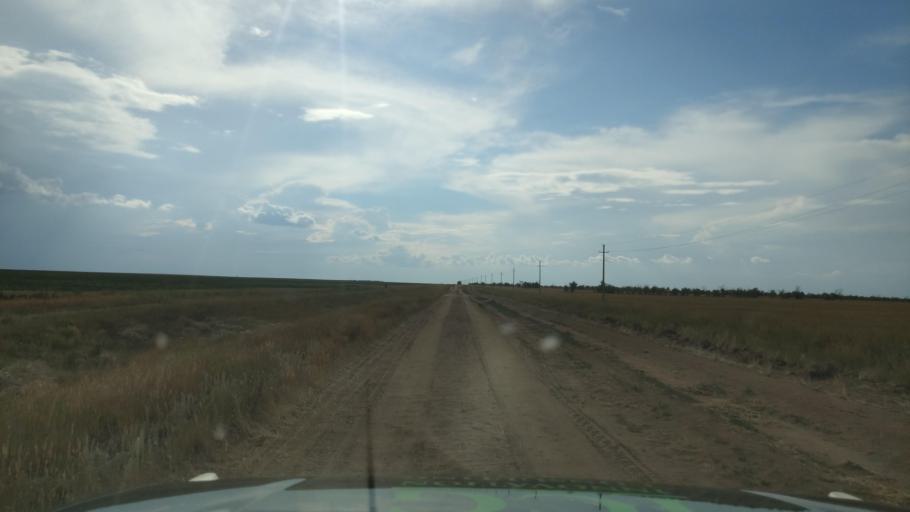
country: KZ
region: Pavlodar
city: Pavlodar
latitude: 52.5126
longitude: 77.4977
